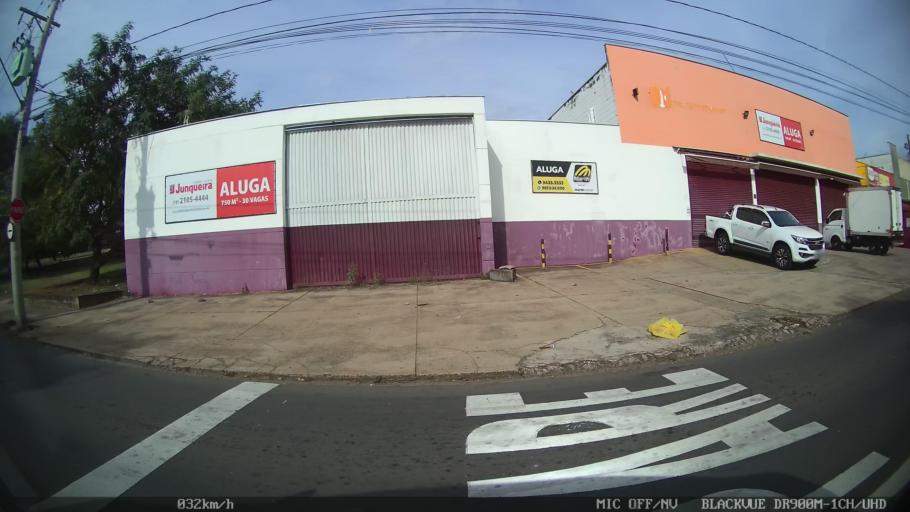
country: BR
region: Sao Paulo
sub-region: Piracicaba
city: Piracicaba
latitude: -22.7452
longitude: -47.6317
